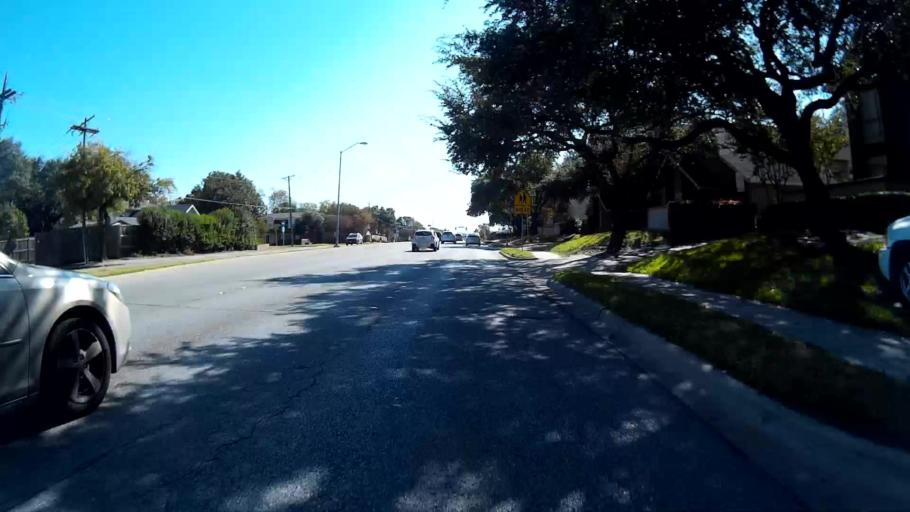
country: US
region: Texas
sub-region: Dallas County
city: Richardson
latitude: 32.9480
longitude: -96.7690
